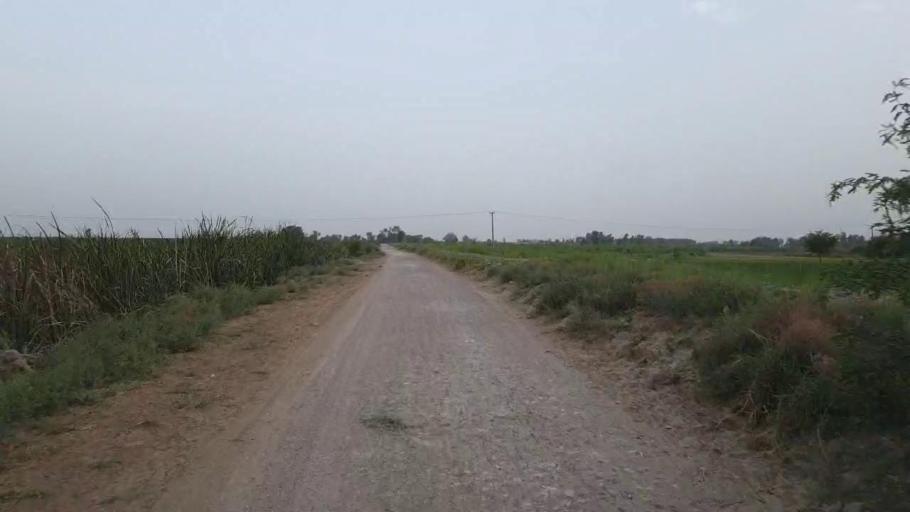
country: PK
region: Sindh
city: Daur
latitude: 26.4087
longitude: 68.2251
